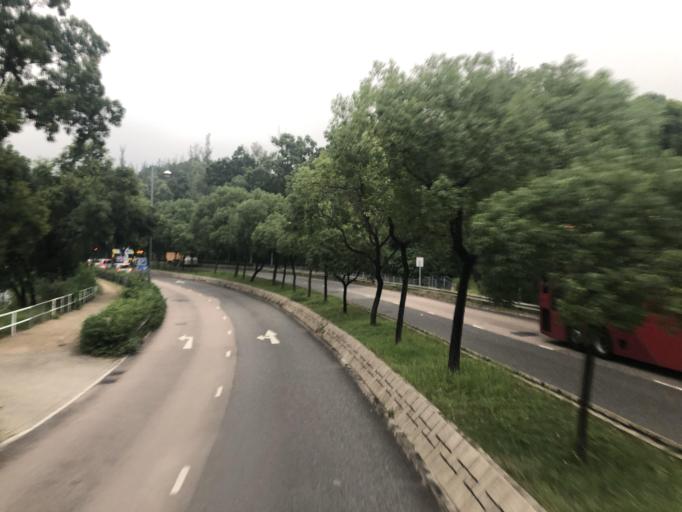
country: HK
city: Tai O
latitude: 22.2892
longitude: 113.9373
